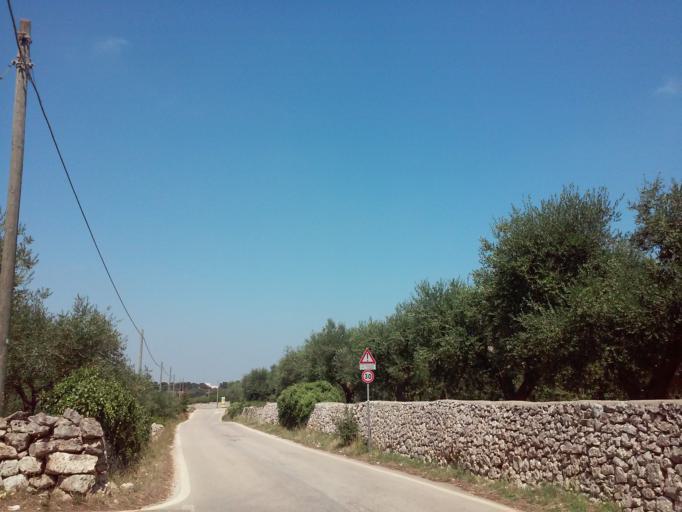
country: IT
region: Apulia
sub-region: Provincia di Bari
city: Alberobello
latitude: 40.7945
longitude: 17.2208
